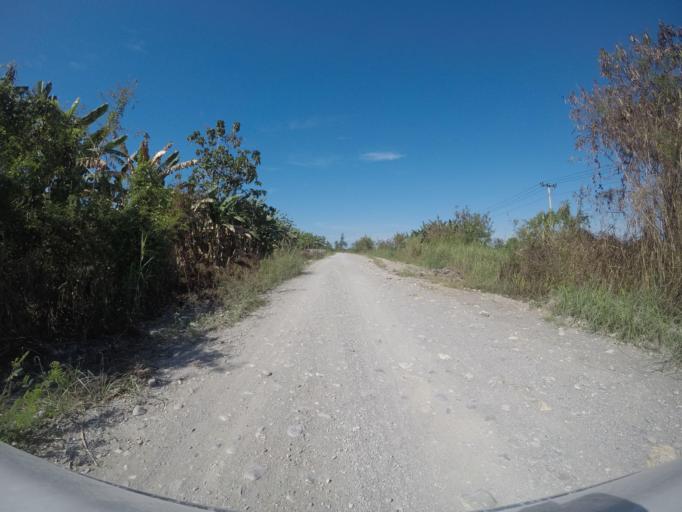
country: TL
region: Viqueque
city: Viqueque
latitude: -8.9436
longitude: 126.1128
